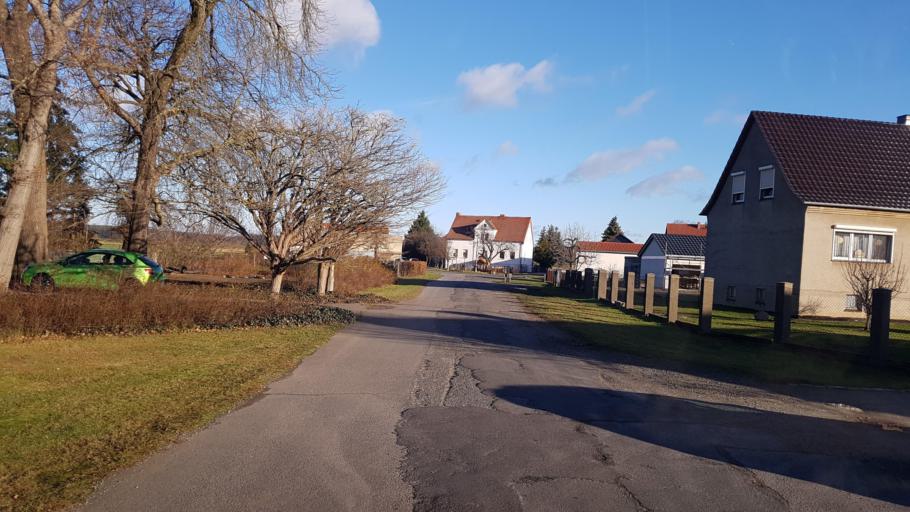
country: DE
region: Brandenburg
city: Forst
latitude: 51.7819
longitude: 14.6475
